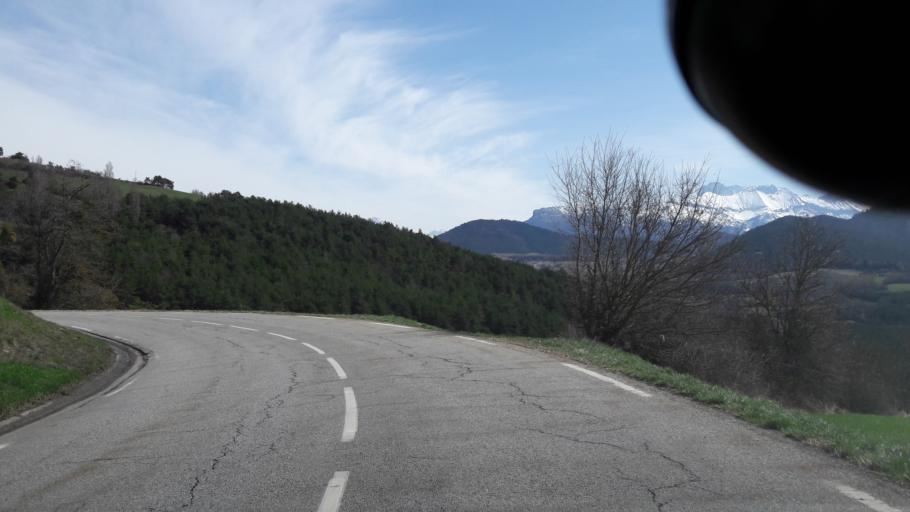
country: FR
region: Rhone-Alpes
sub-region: Departement de l'Isere
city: La Motte-Saint-Martin
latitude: 44.8724
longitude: 5.6524
